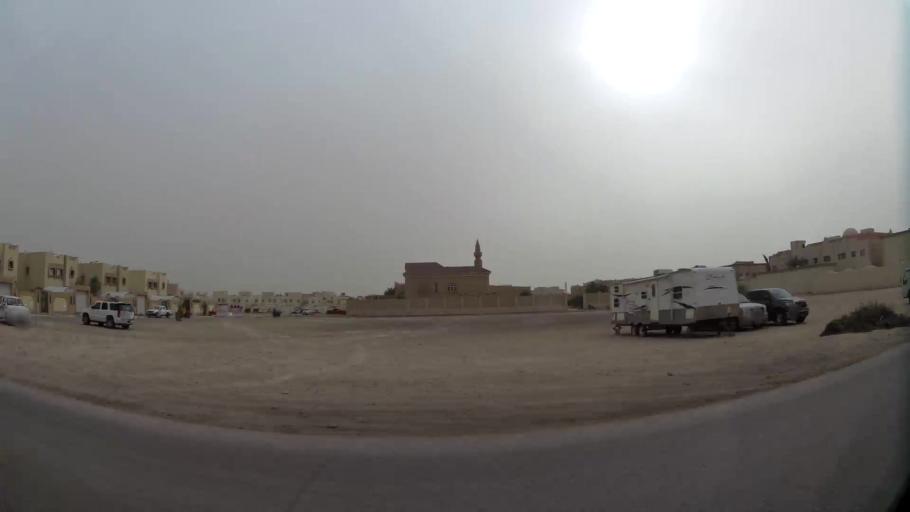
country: QA
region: Baladiyat ad Dawhah
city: Doha
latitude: 25.2459
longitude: 51.4976
